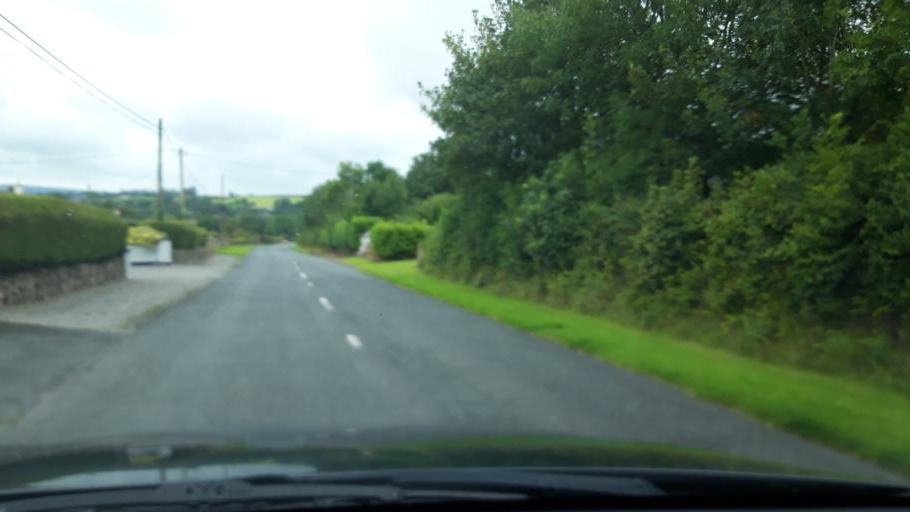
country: IE
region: Munster
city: Cahir
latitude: 52.1784
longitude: -7.8497
